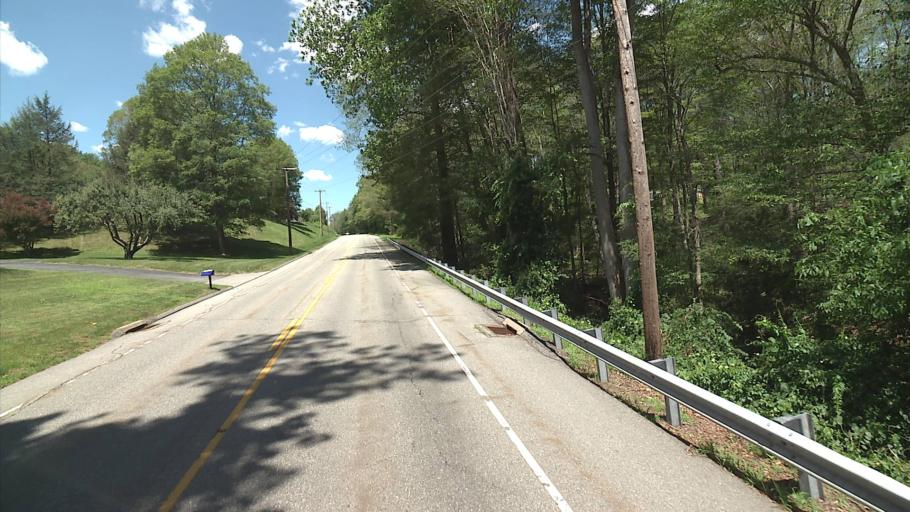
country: US
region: Connecticut
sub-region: Middlesex County
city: Moodus
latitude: 41.5002
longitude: -72.4690
